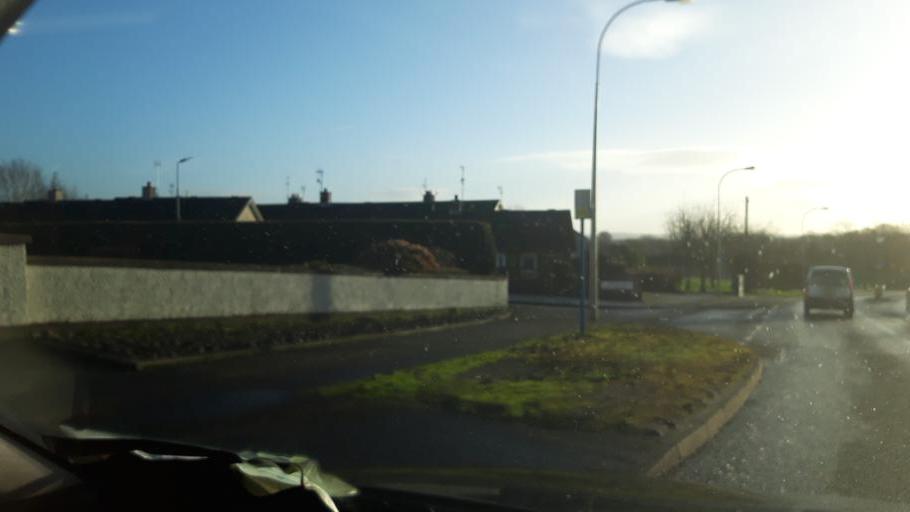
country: GB
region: Northern Ireland
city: Maghera
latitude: 54.8429
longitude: -6.6757
